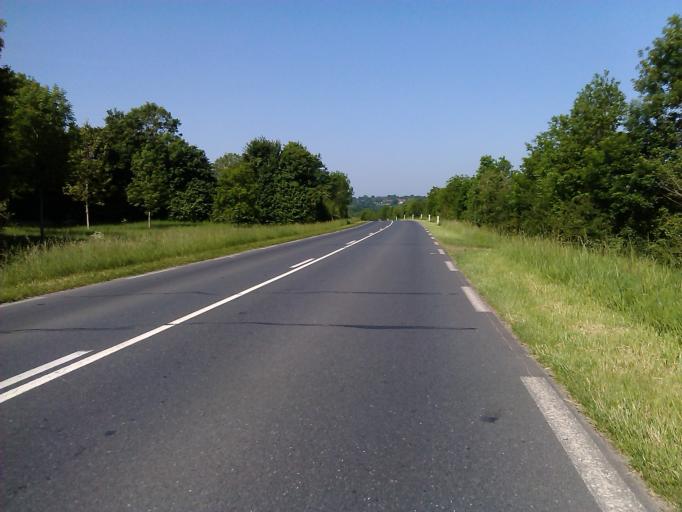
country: FR
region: Centre
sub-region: Departement de l'Indre
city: Neuvy-Saint-Sepulchre
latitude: 46.5994
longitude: 1.7530
